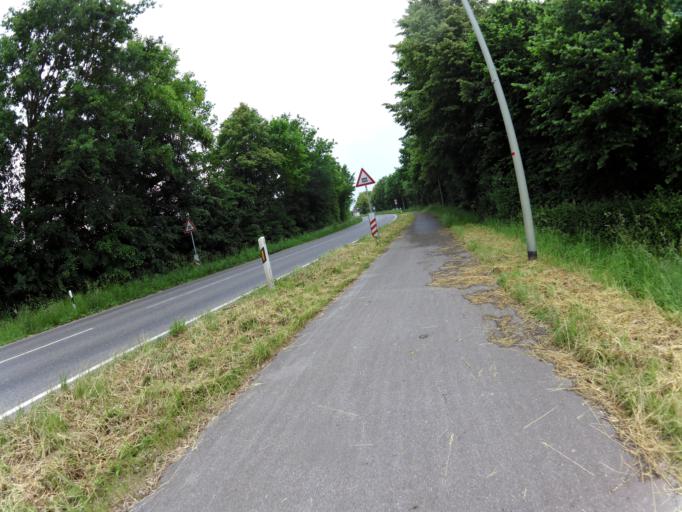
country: DE
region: North Rhine-Westphalia
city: Geilenkirchen
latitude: 50.9880
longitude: 6.1789
